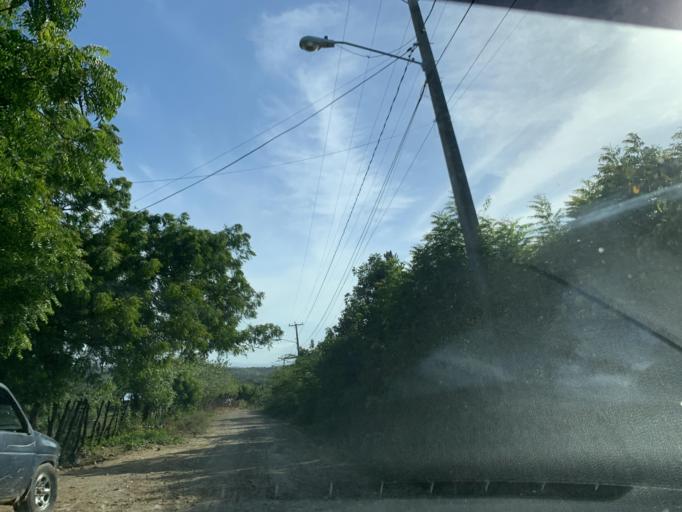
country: DO
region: Puerto Plata
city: Luperon
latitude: 19.8845
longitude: -70.9209
